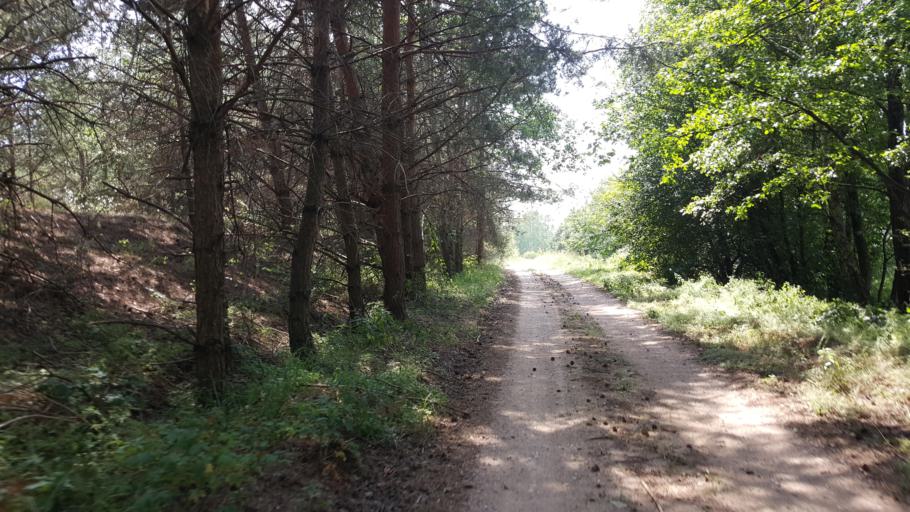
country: BY
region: Brest
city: Kamyanyets
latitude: 52.3684
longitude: 23.7473
